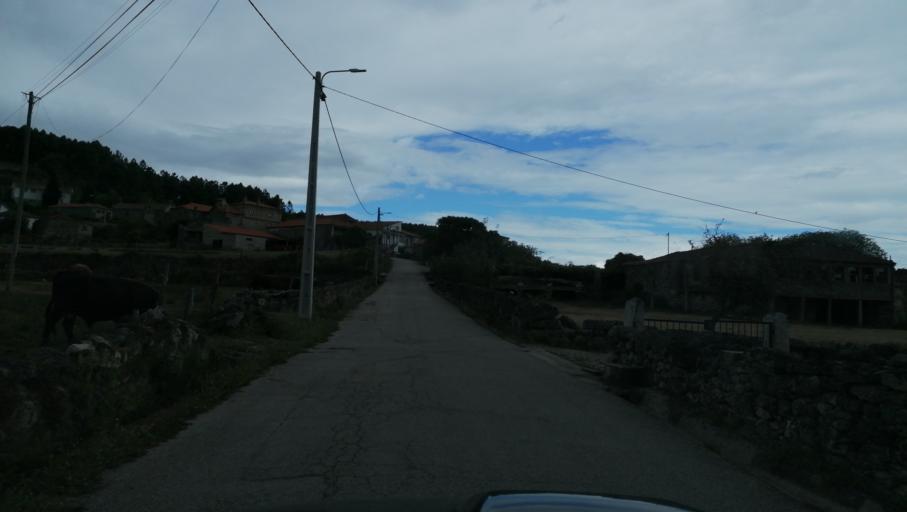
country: PT
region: Vila Real
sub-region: Vila Pouca de Aguiar
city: Vila Pouca de Aguiar
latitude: 41.5608
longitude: -7.6519
